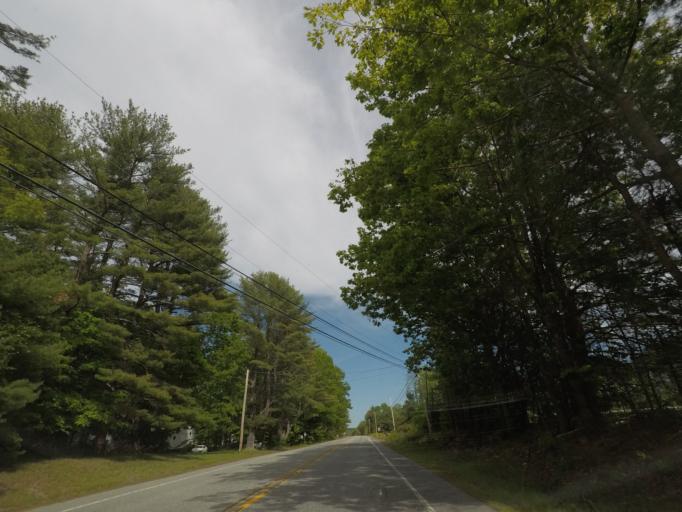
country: US
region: Maine
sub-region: Sagadahoc County
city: Richmond
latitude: 44.0876
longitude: -69.7707
